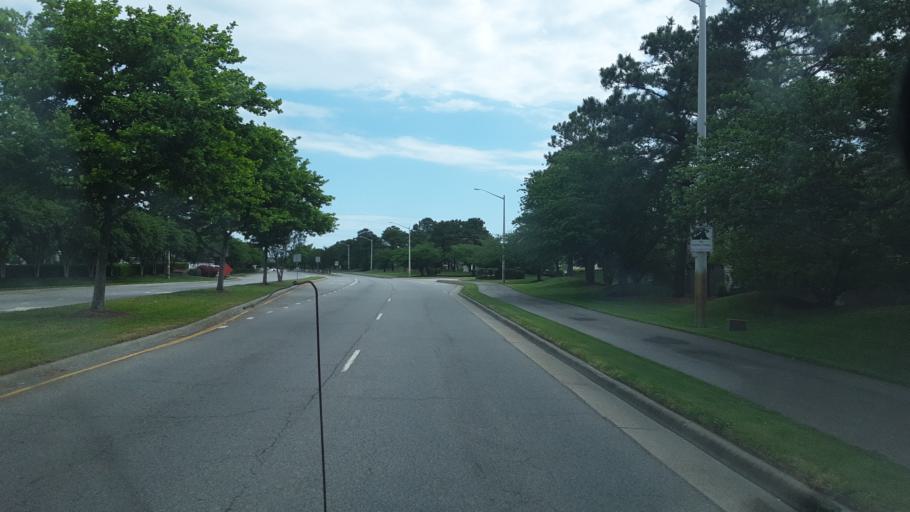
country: US
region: Virginia
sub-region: City of Virginia Beach
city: Virginia Beach
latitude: 36.7528
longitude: -76.0090
